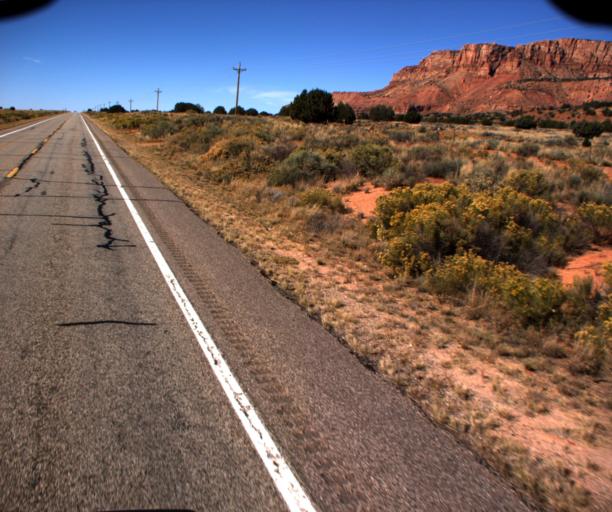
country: US
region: Arizona
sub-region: Mohave County
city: Colorado City
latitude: 36.8582
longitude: -112.7891
